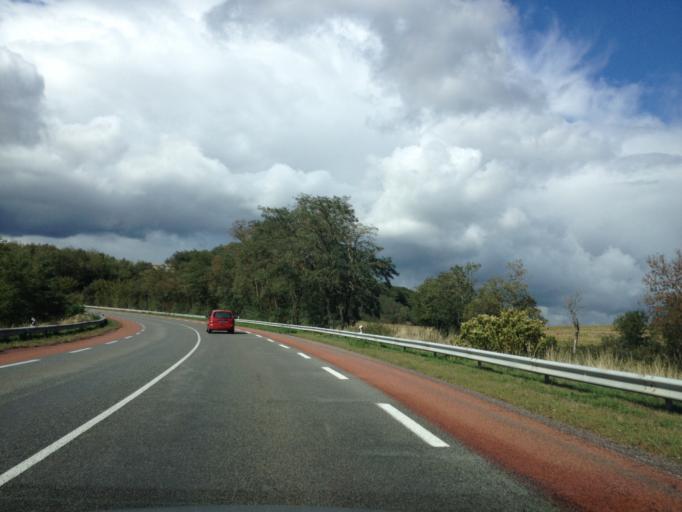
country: FR
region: Rhone-Alpes
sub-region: Departement du Rhone
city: Amplepuis
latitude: 45.9415
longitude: 4.2917
